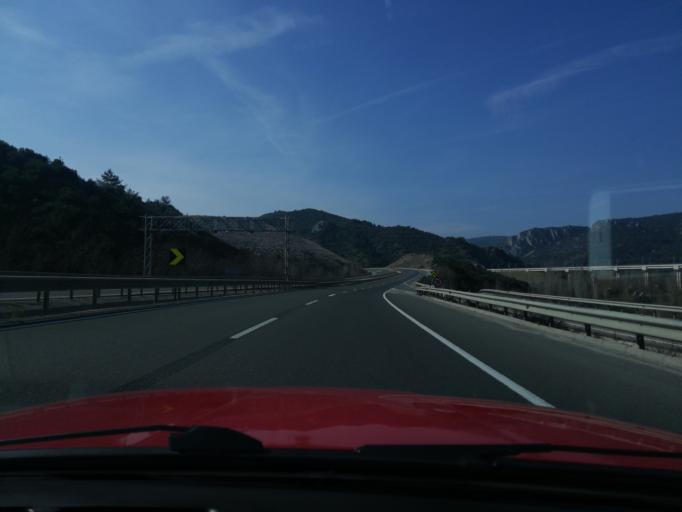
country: TR
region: Bilecik
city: Bilecik
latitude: 40.1618
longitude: 30.0207
